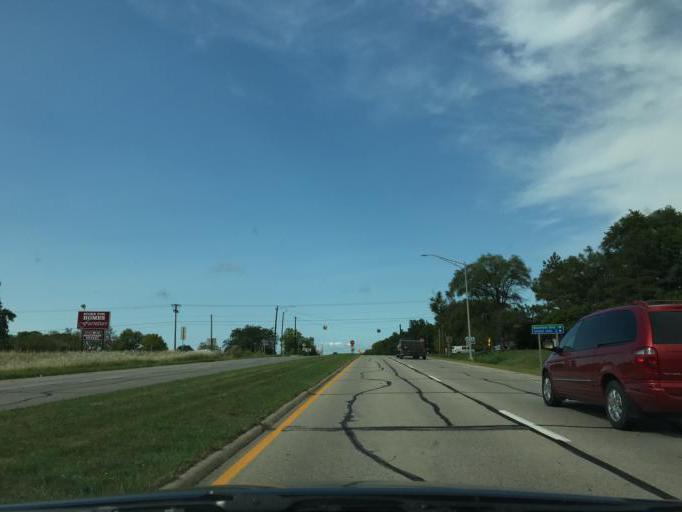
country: US
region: Iowa
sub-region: Jasper County
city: Newton
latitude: 41.6977
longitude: -93.0759
